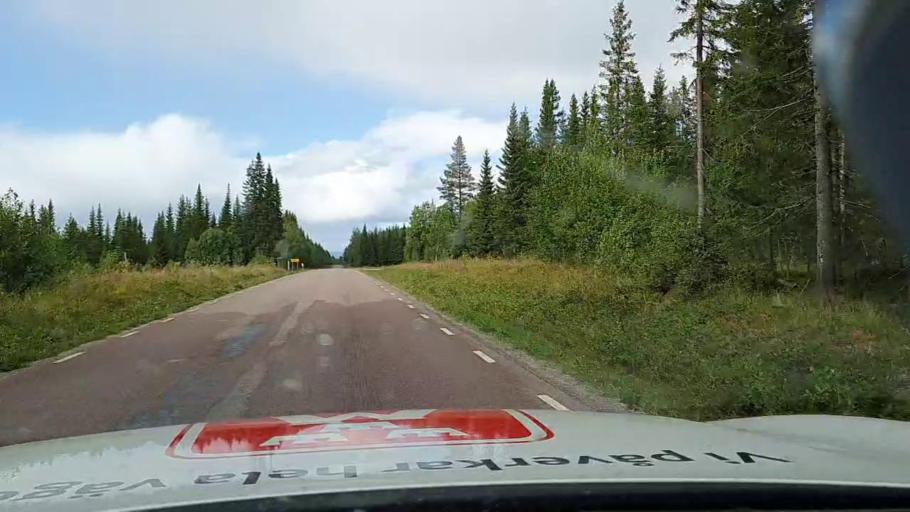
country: SE
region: Jaemtland
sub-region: Stroemsunds Kommun
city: Stroemsund
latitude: 63.8703
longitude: 15.3705
